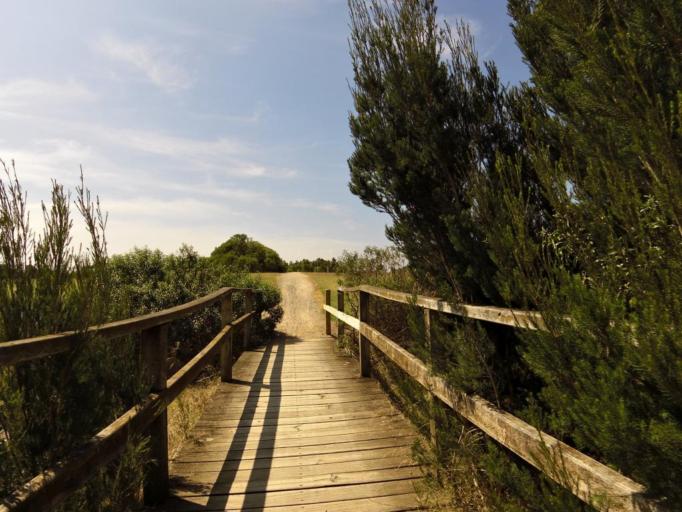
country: AU
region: Victoria
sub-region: Mornington Peninsula
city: Hastings
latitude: -38.3136
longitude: 145.1949
